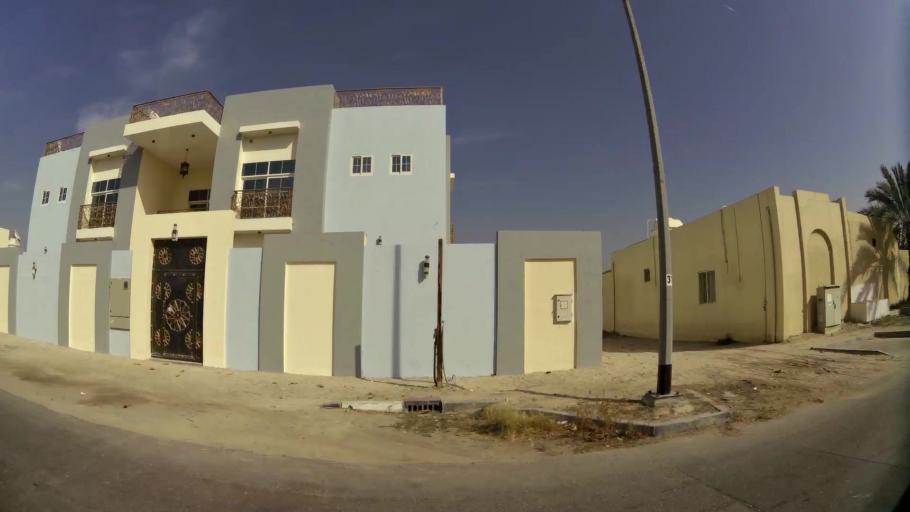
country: AE
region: Ash Shariqah
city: Sharjah
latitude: 25.2591
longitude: 55.3963
